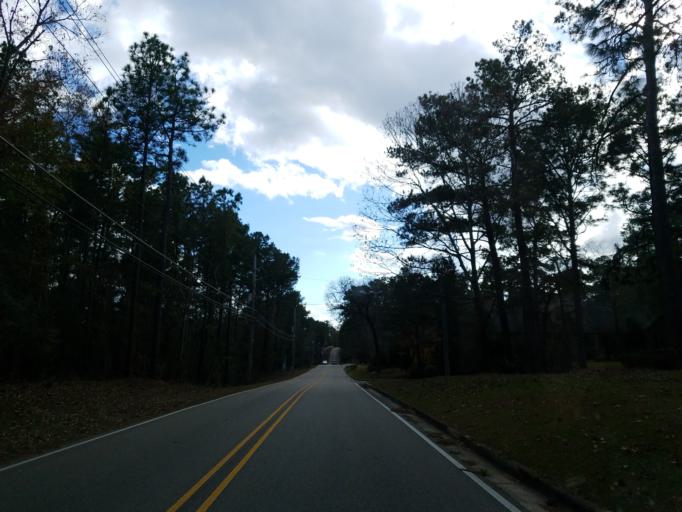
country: US
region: Mississippi
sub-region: Lamar County
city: West Hattiesburg
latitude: 31.2913
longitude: -89.3478
